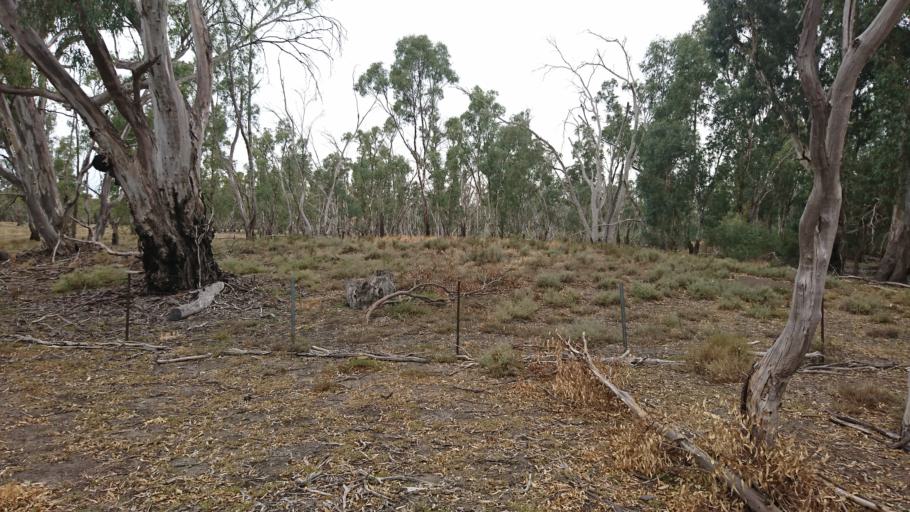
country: AU
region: Victoria
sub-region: Swan Hill
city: Swan Hill
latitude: -35.1395
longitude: 143.3772
